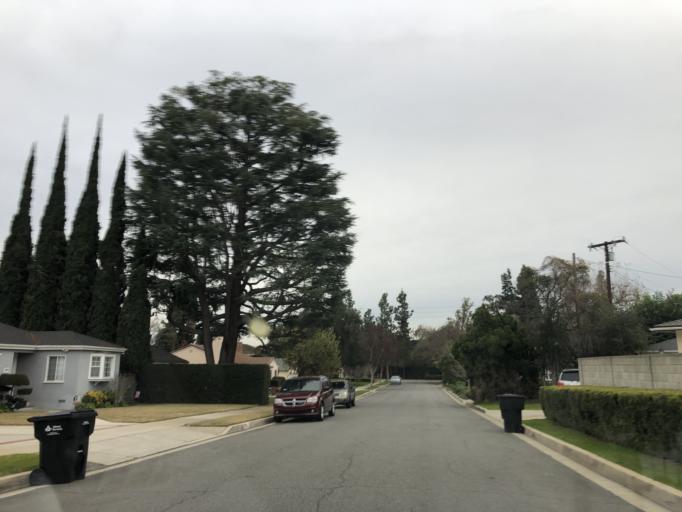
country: US
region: California
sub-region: Los Angeles County
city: San Marino
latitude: 34.1147
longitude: -118.0984
